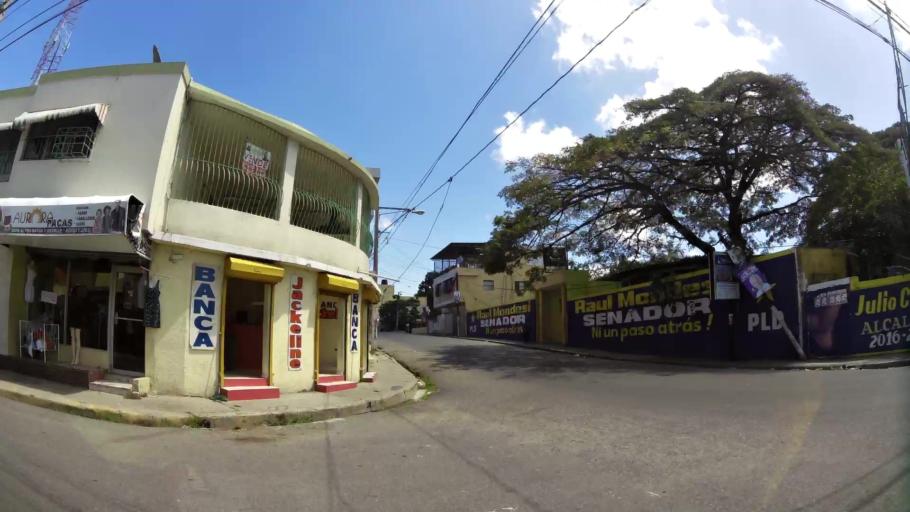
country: DO
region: San Cristobal
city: San Cristobal
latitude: 18.4097
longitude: -70.1078
